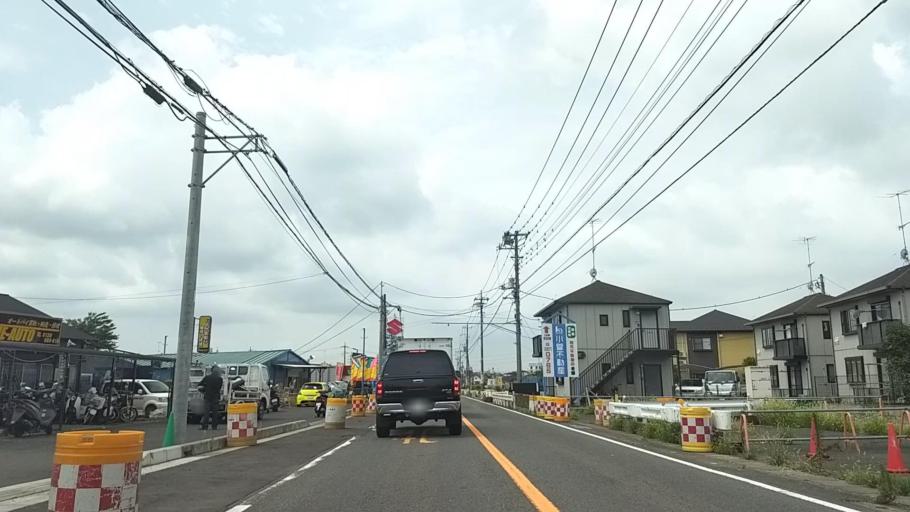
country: JP
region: Kanagawa
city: Minami-rinkan
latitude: 35.4525
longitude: 139.4726
